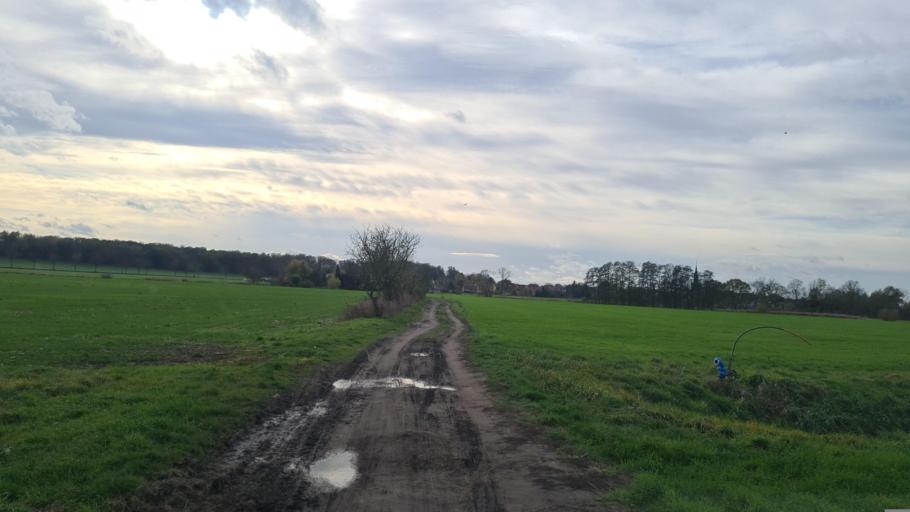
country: DE
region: Brandenburg
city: Schlieben
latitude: 51.7288
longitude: 13.3938
